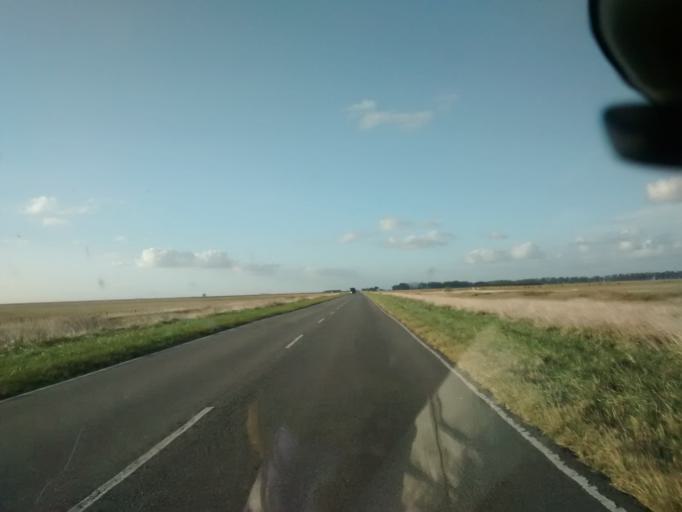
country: AR
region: Buenos Aires
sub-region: Partido de General Belgrano
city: General Belgrano
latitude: -36.0633
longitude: -58.6256
